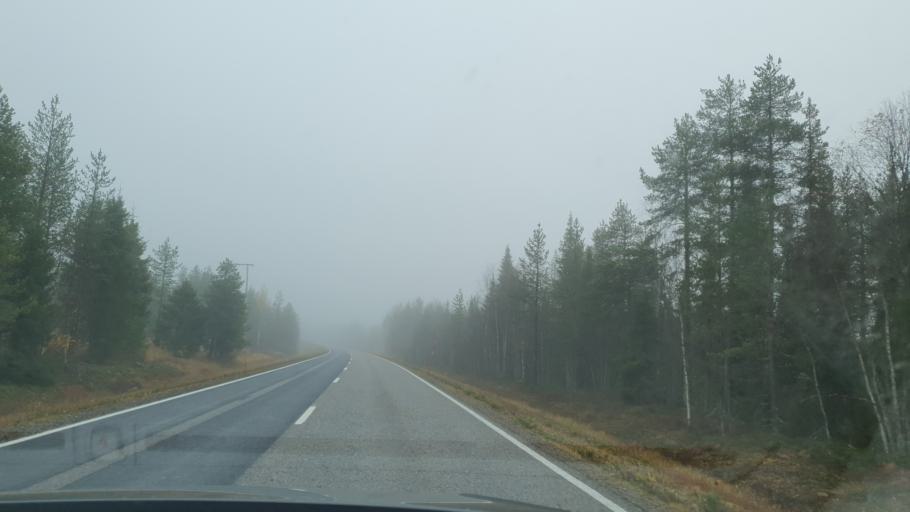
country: FI
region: Lapland
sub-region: Tunturi-Lappi
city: Kittilae
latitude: 67.2606
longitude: 24.8913
